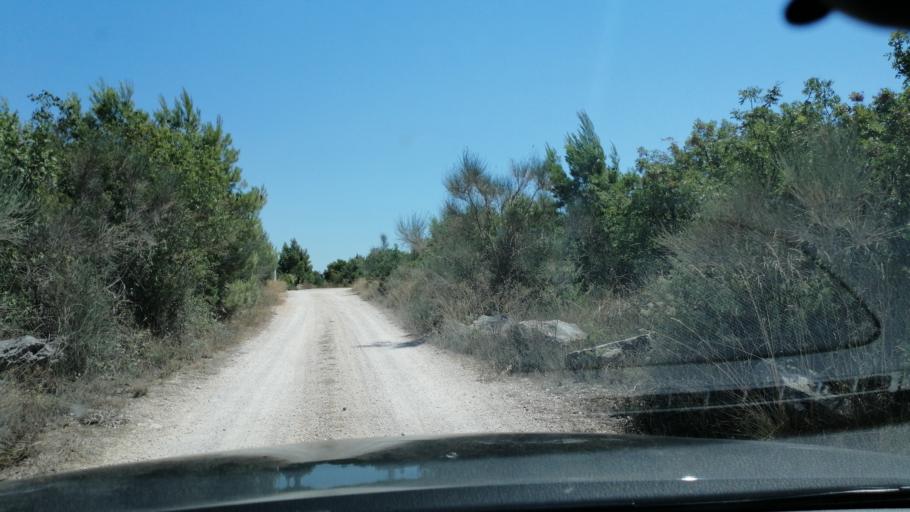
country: HR
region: Sibensko-Kniniska
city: Murter
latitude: 43.8455
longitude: 15.6273
